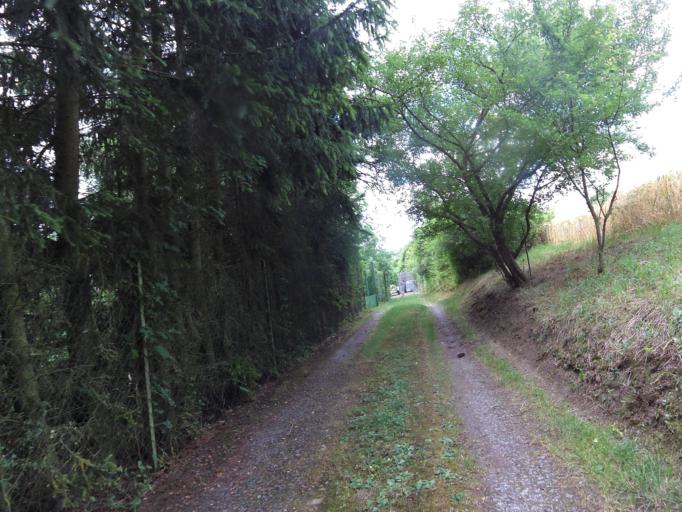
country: DE
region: Bavaria
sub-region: Regierungsbezirk Unterfranken
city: Randersacker
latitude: 49.7731
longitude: 9.9669
